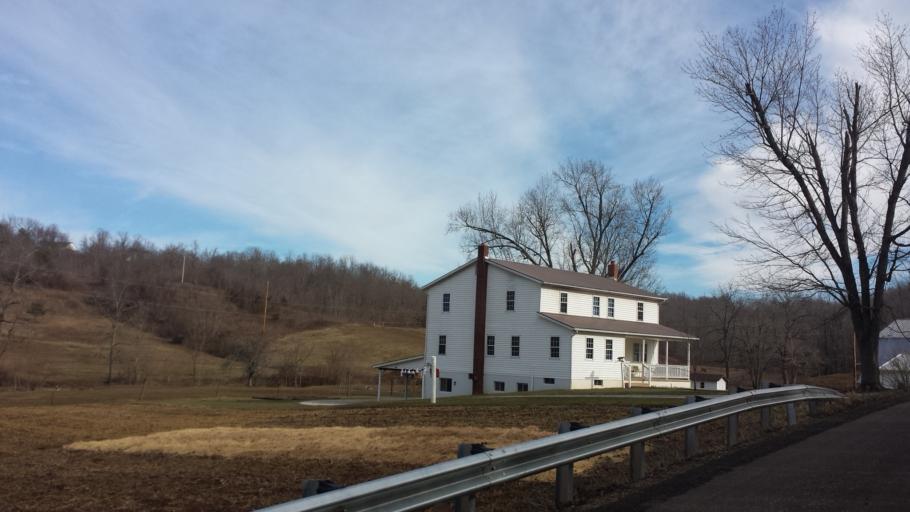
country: US
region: Ohio
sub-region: Gallia County
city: Gallipolis
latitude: 38.7215
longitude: -82.3519
